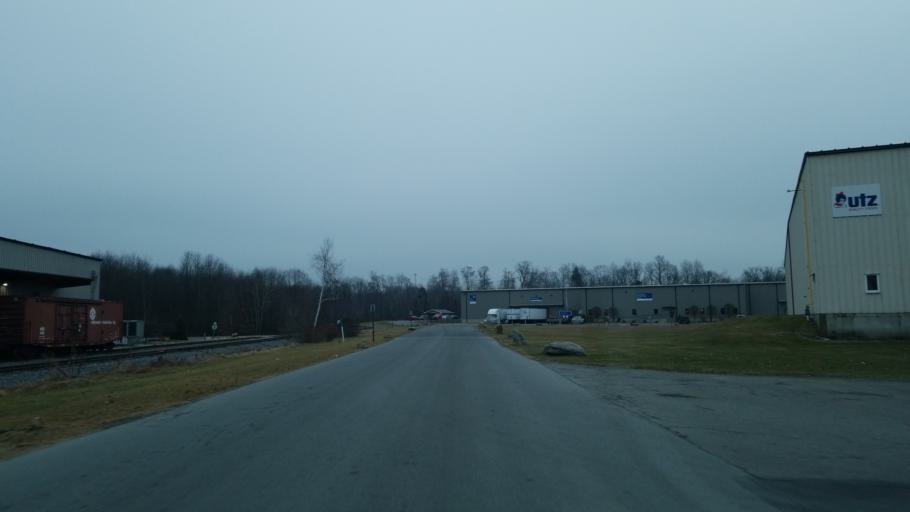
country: US
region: Pennsylvania
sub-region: Clearfield County
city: DuBois
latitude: 41.1163
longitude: -78.7290
